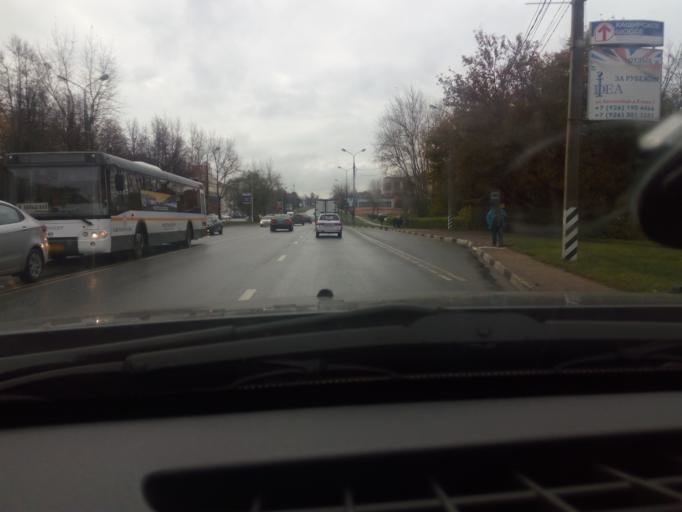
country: RU
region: Moskovskaya
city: Domodedovo
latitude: 55.4502
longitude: 37.7630
